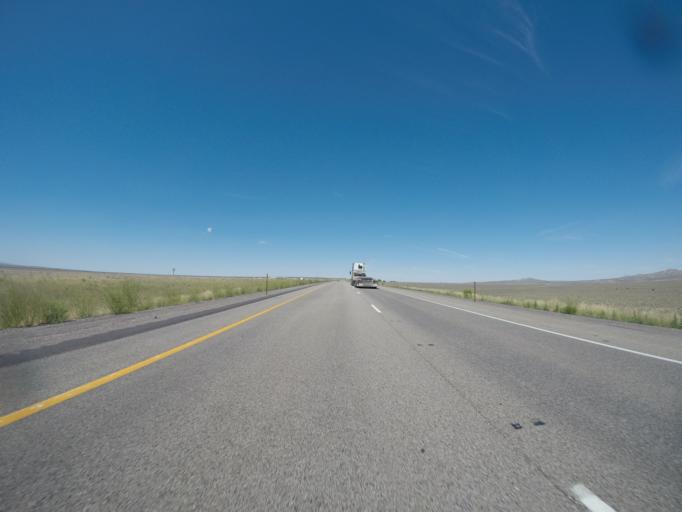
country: US
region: Wyoming
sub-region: Carbon County
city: Saratoga
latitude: 41.7422
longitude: -106.8031
